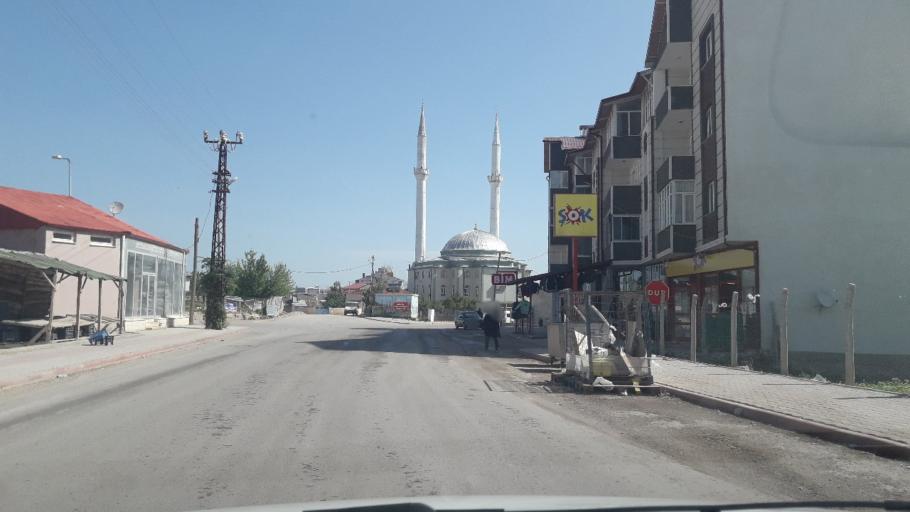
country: TR
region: Sivas
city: Kangal
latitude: 39.2313
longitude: 37.3886
